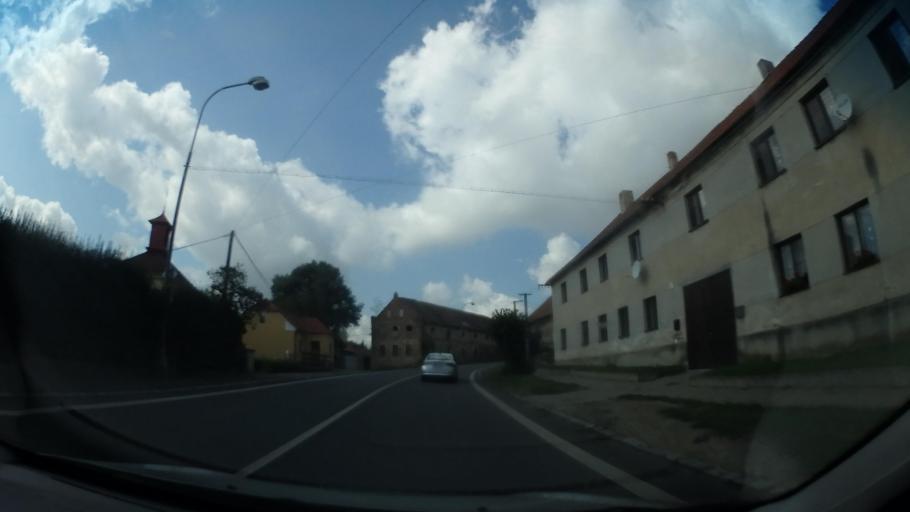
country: CZ
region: Central Bohemia
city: Cervene Pecky
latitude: 49.9464
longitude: 15.2047
